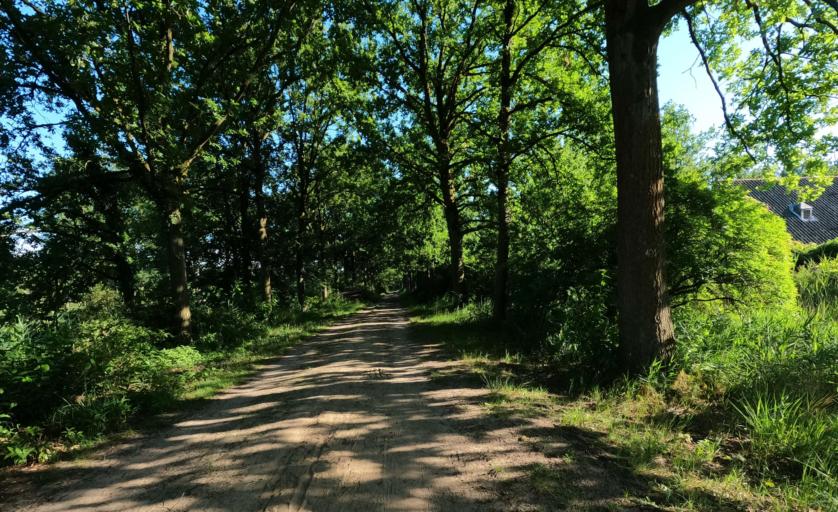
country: BE
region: Flanders
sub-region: Provincie Antwerpen
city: Schilde
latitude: 51.2603
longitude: 4.5707
